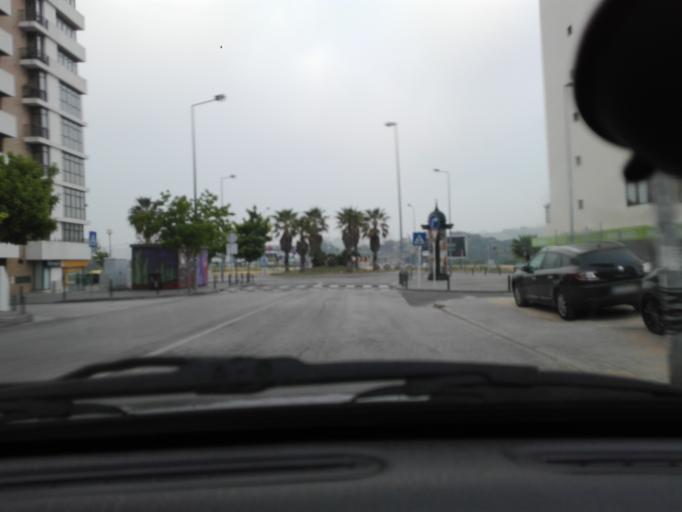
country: PT
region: Lisbon
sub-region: Loures
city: Loures
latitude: 38.8385
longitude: -9.1587
